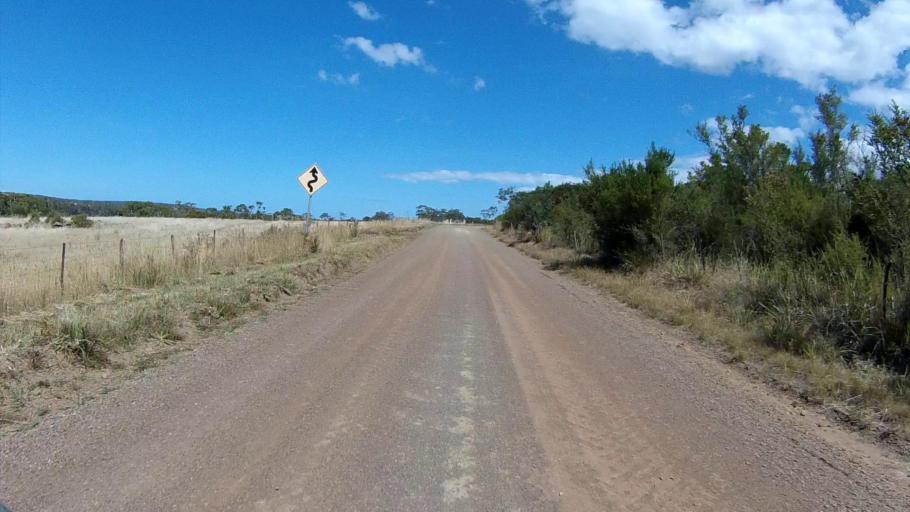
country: AU
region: Tasmania
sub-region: Break O'Day
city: St Helens
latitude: -41.9693
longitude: 148.0733
